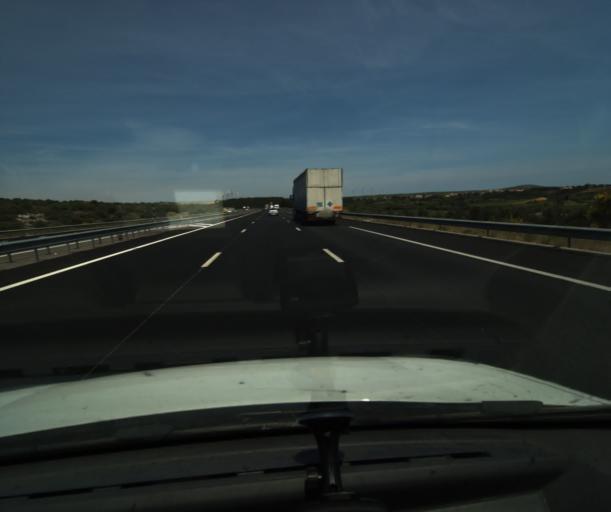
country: FR
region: Languedoc-Roussillon
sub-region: Departement de l'Aude
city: Sigean
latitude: 42.9726
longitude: 2.9714
